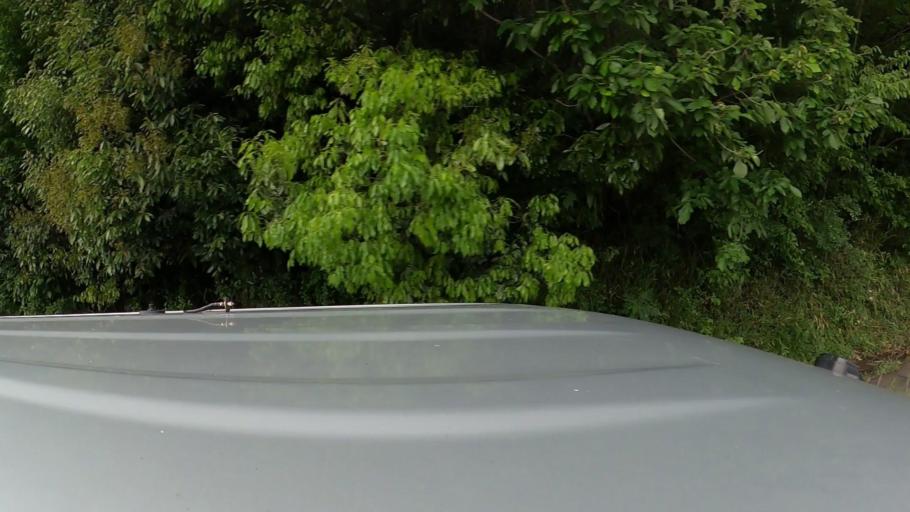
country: JP
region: Ibaraki
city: Ushiku
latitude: 35.9656
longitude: 140.1999
